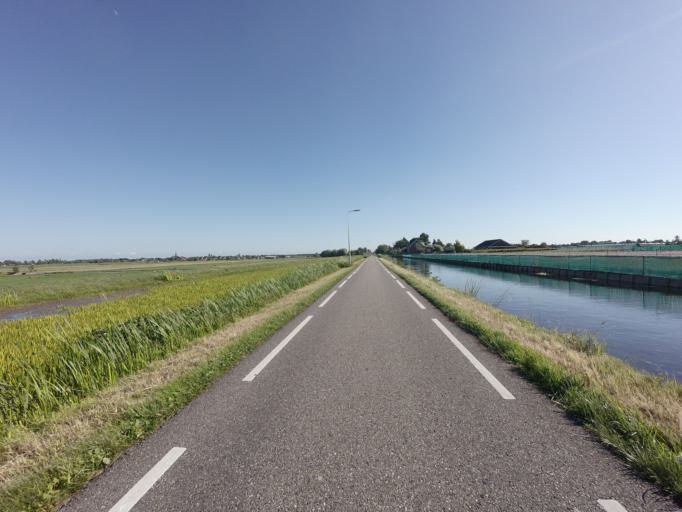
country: NL
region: South Holland
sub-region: Gemeente Boskoop
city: Boskoop
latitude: 52.0659
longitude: 4.6843
